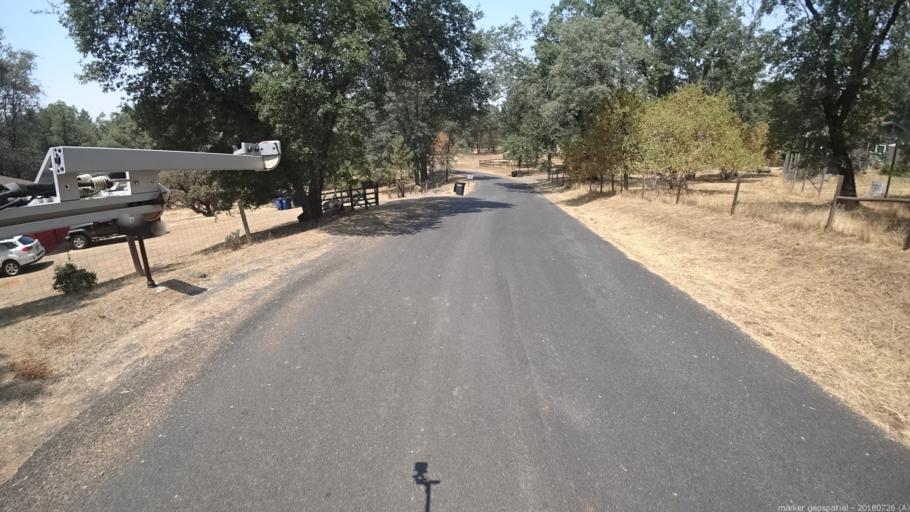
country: US
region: California
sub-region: Madera County
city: Oakhurst
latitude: 37.2828
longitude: -119.6321
